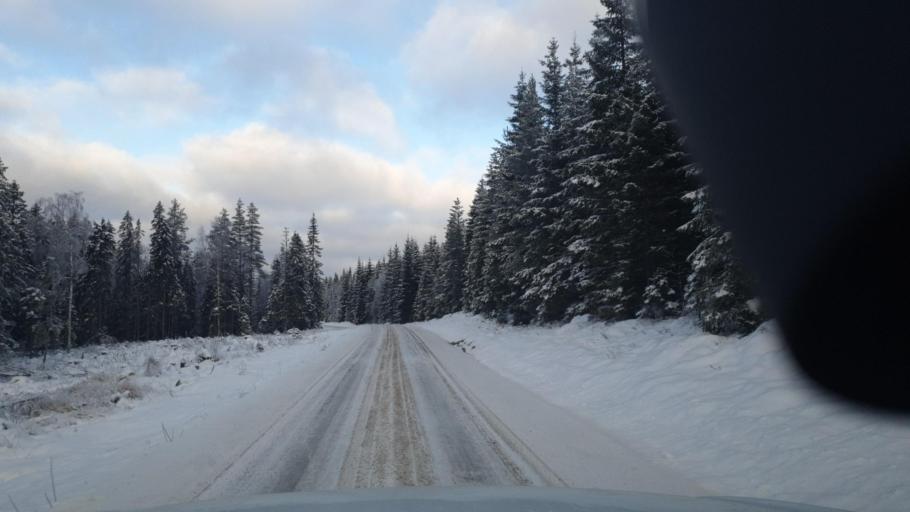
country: SE
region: Vaermland
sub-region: Eda Kommun
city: Charlottenberg
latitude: 60.0751
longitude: 12.6206
